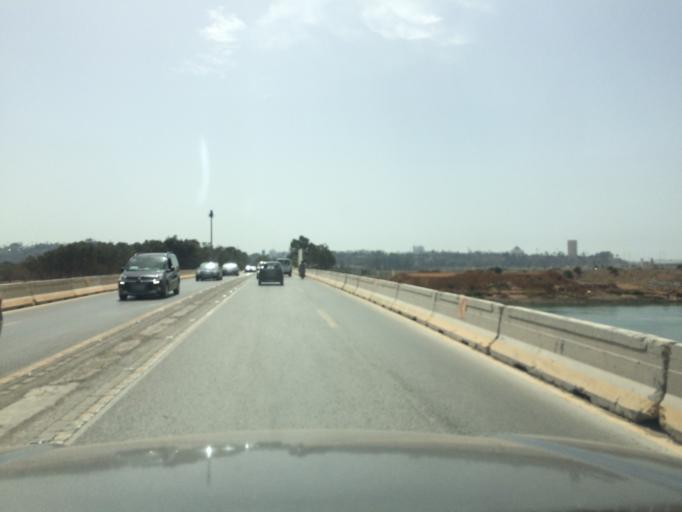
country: MA
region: Rabat-Sale-Zemmour-Zaer
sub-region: Rabat
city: Rabat
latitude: 34.0200
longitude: -6.8060
